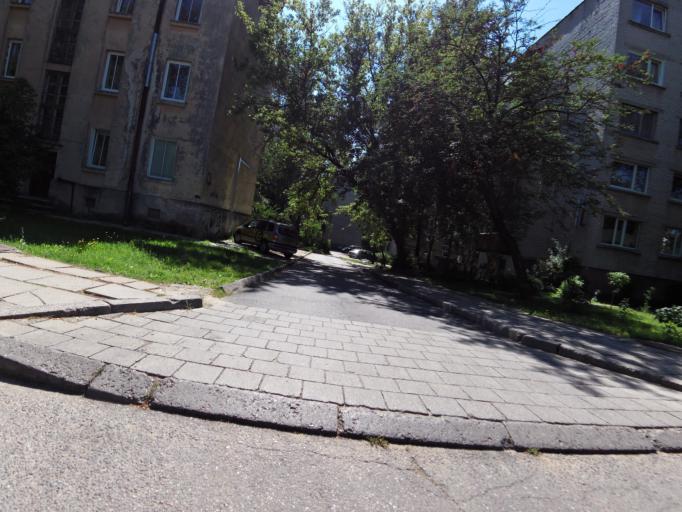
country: LT
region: Vilnius County
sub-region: Vilnius
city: Vilnius
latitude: 54.6988
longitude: 25.2902
